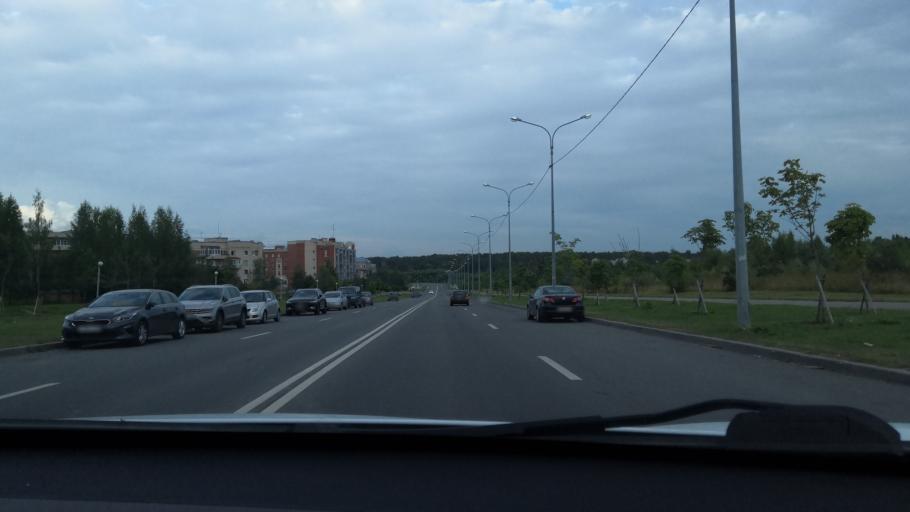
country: RU
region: St.-Petersburg
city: Pavlovsk
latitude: 59.6946
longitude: 30.4185
